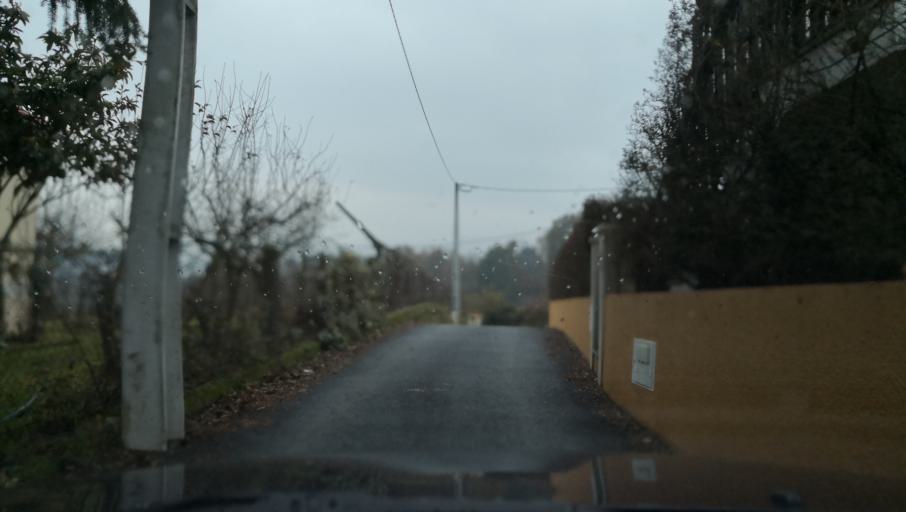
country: PT
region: Vila Real
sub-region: Vila Real
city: Vila Real
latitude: 41.3062
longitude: -7.7726
